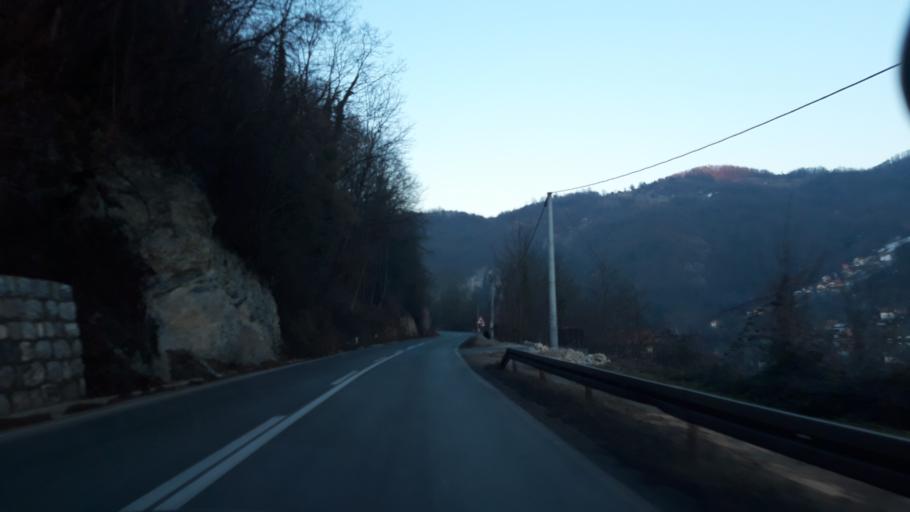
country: RS
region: Central Serbia
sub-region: Macvanski Okrug
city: Mali Zvornik
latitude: 44.3324
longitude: 19.1302
